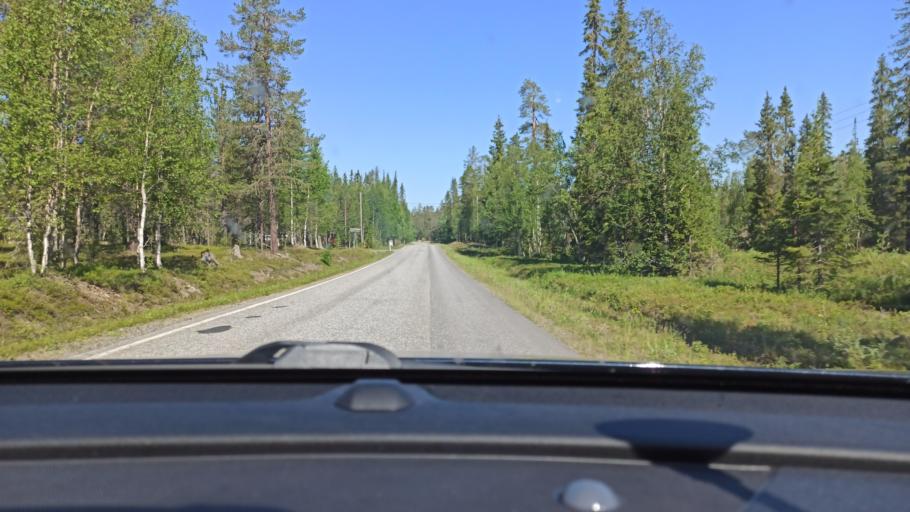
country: FI
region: Lapland
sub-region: Tunturi-Lappi
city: Kolari
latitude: 67.6659
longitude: 24.1609
